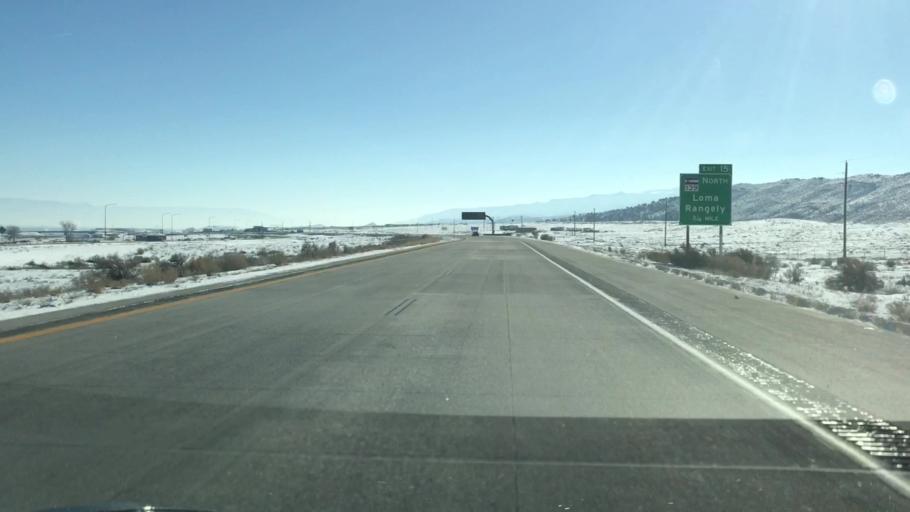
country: US
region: Colorado
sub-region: Mesa County
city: Loma
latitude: 39.1823
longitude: -108.8293
